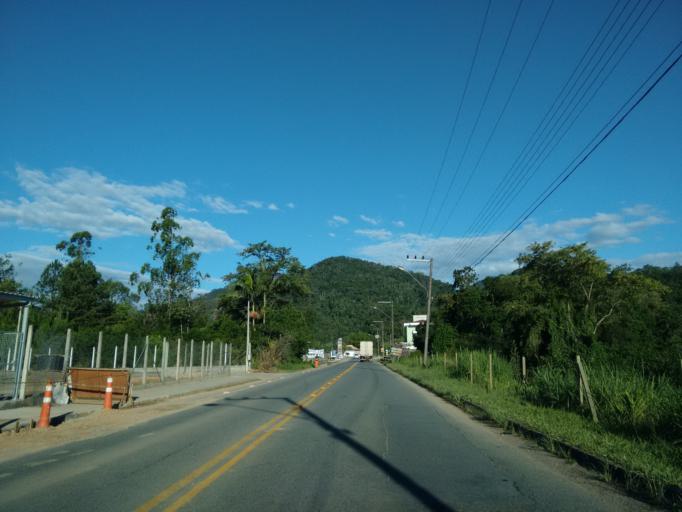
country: BR
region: Santa Catarina
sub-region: Pomerode
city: Pomerode
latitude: -26.7511
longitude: -49.1712
